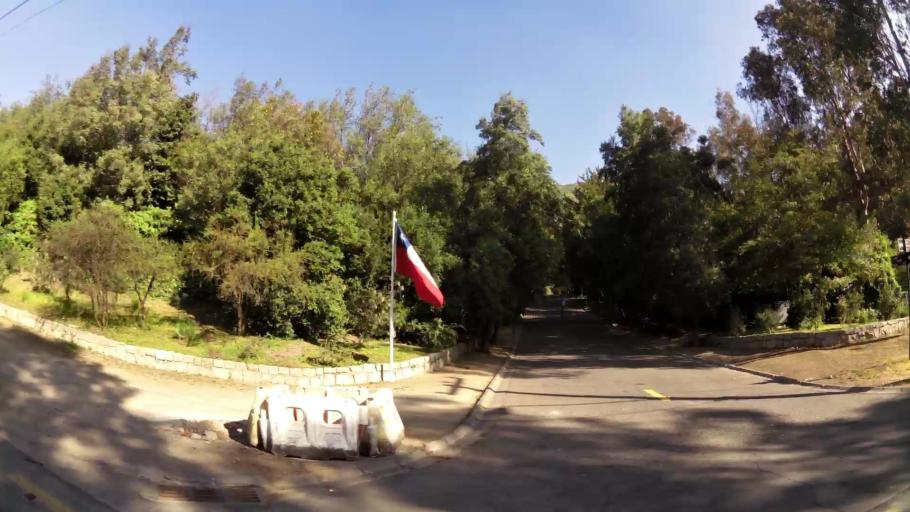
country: CL
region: Santiago Metropolitan
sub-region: Provincia de Santiago
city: Villa Presidente Frei, Nunoa, Santiago, Chile
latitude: -33.3650
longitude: -70.4827
